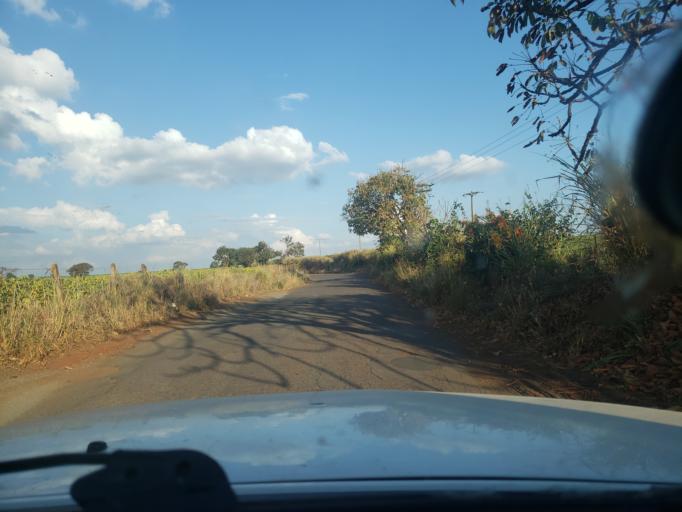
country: BR
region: Sao Paulo
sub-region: Mogi-Mirim
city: Mogi Mirim
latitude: -22.4698
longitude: -46.9296
